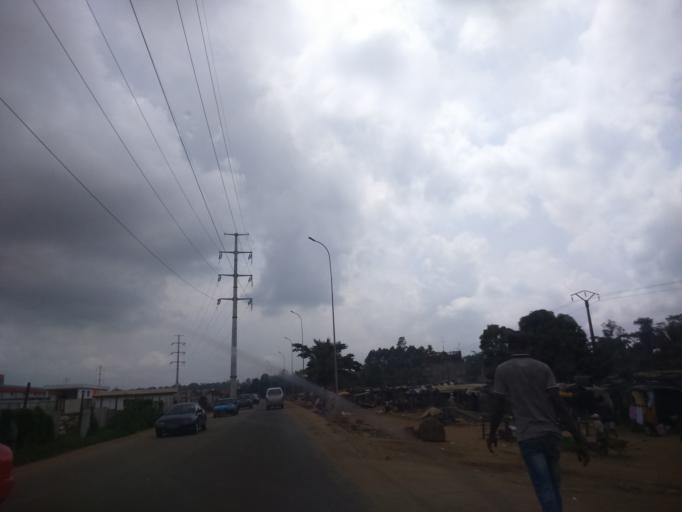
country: CI
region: Lagunes
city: Abobo
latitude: 5.3810
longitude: -4.0756
